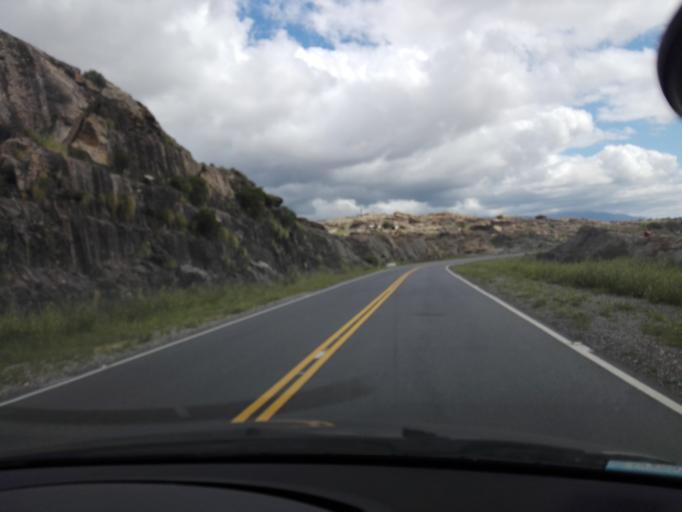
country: AR
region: Cordoba
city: Mina Clavero
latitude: -31.7309
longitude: -64.9007
